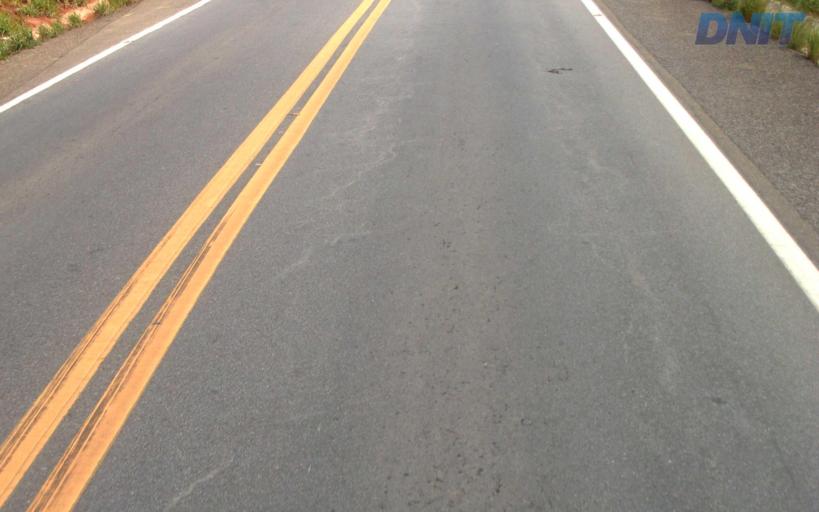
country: BR
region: Minas Gerais
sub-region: Belo Oriente
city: Belo Oriente
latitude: -19.1205
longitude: -42.2132
